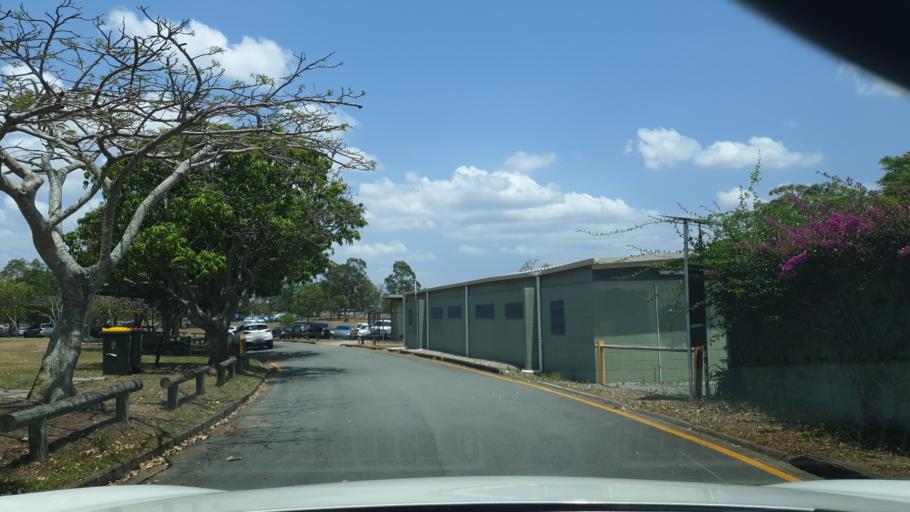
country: AU
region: Queensland
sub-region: Brisbane
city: Chermside West
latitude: -27.3757
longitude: 153.0309
